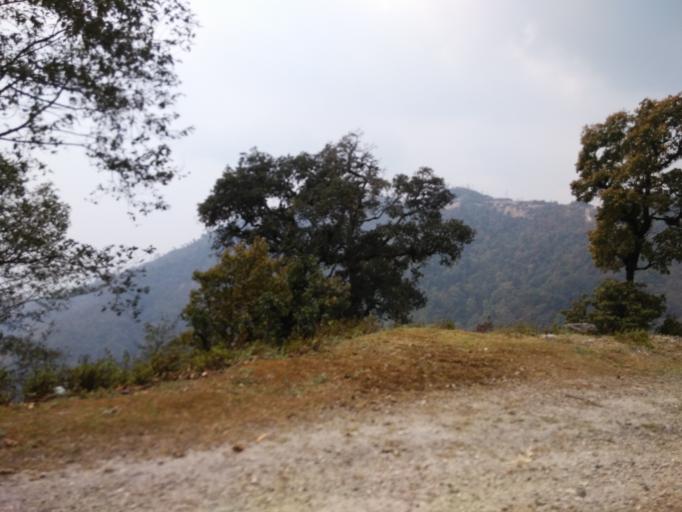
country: NP
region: Central Region
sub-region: Narayani Zone
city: Hitura
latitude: 27.5677
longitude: 85.0732
